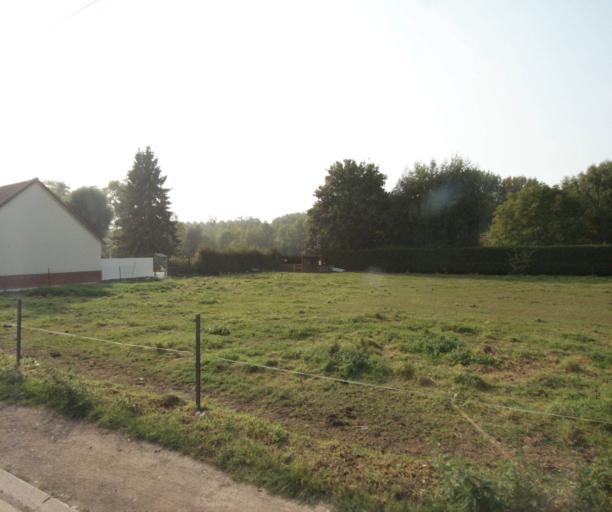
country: FR
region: Nord-Pas-de-Calais
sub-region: Departement du Nord
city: Emmerin
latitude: 50.5857
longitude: 2.9974
